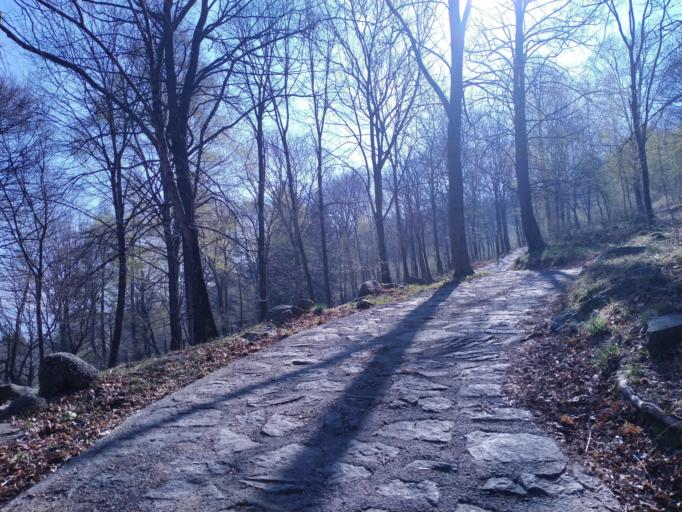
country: IT
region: Lombardy
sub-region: Provincia di Como
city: Rezzago
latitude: 45.8557
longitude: 9.2392
